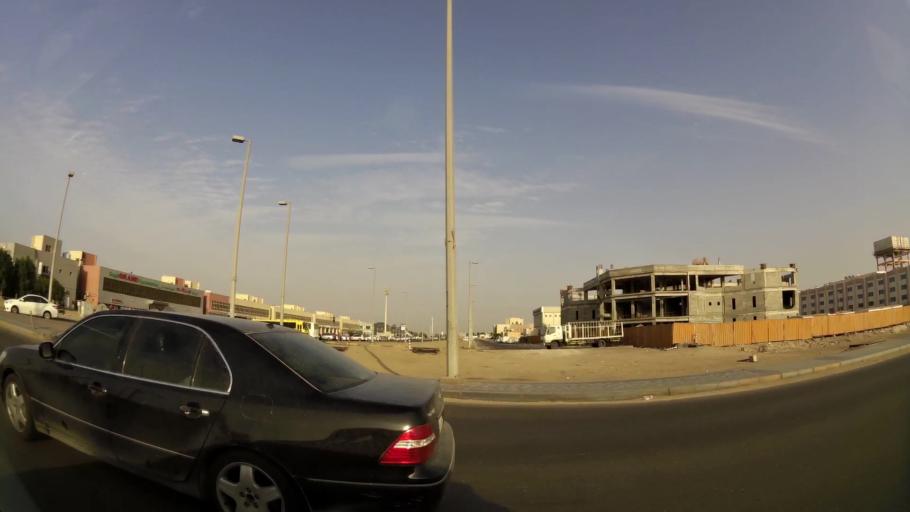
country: AE
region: Abu Dhabi
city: Abu Dhabi
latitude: 24.3642
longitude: 54.5164
